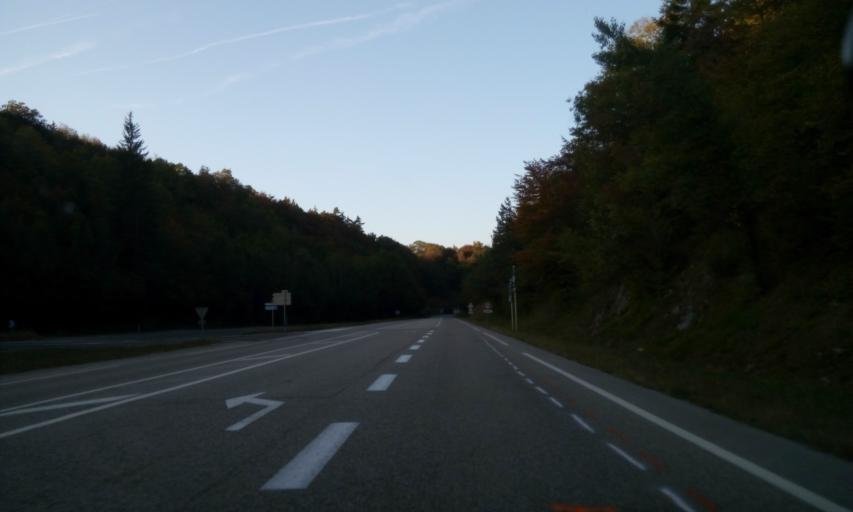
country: FR
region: Rhone-Alpes
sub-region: Departement de l'Ain
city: Saint-Martin-du-Frene
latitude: 46.1139
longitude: 5.4972
